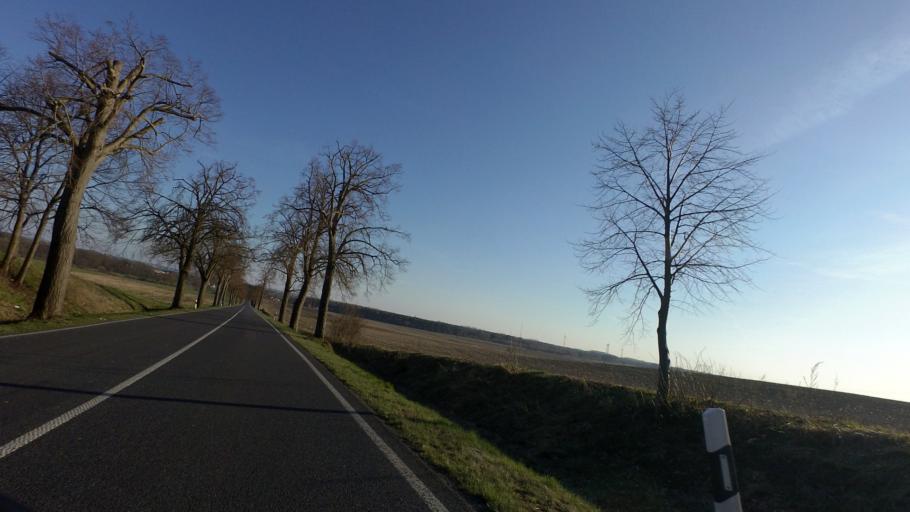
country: DE
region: Brandenburg
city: Britz
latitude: 52.8985
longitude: 13.8029
